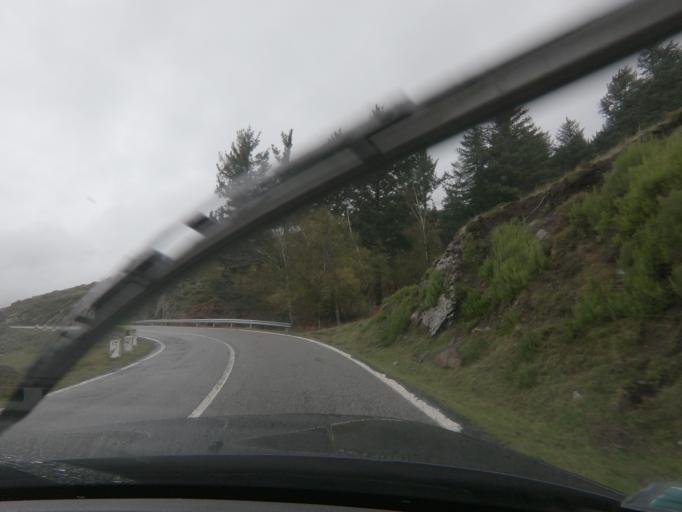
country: PT
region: Vila Real
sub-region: Mondim de Basto
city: Mondim de Basto
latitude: 41.3225
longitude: -7.8864
